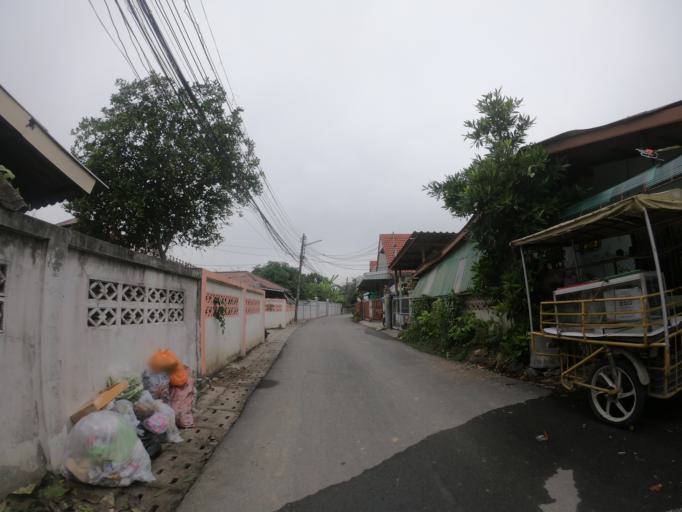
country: TH
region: Chiang Mai
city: Hang Dong
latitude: 18.7430
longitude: 98.9452
